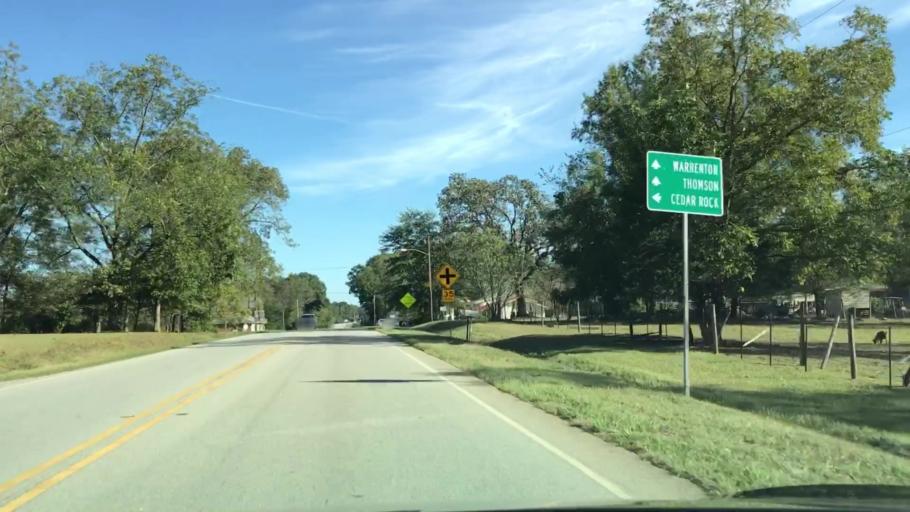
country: US
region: Georgia
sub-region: Warren County
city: Firing Range
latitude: 33.4627
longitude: -82.7082
